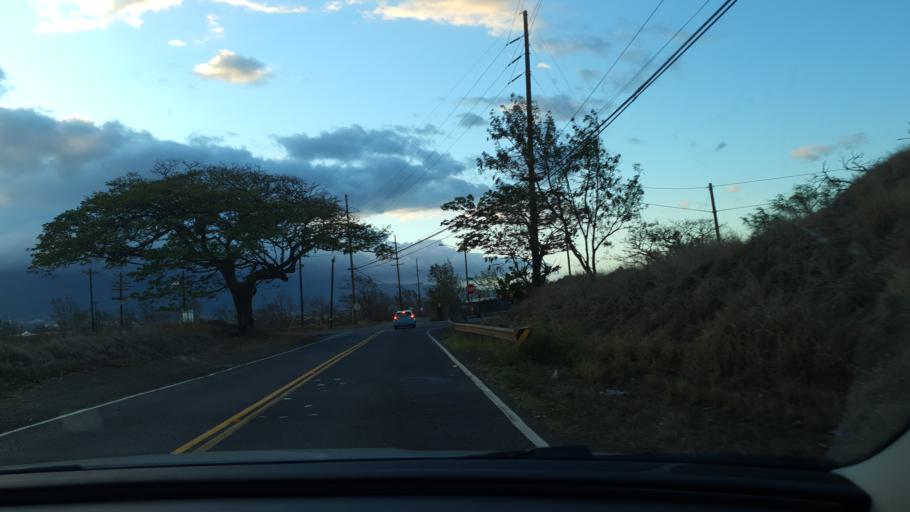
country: US
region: Hawaii
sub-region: Maui County
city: Kahului
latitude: 20.8721
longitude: -156.4392
